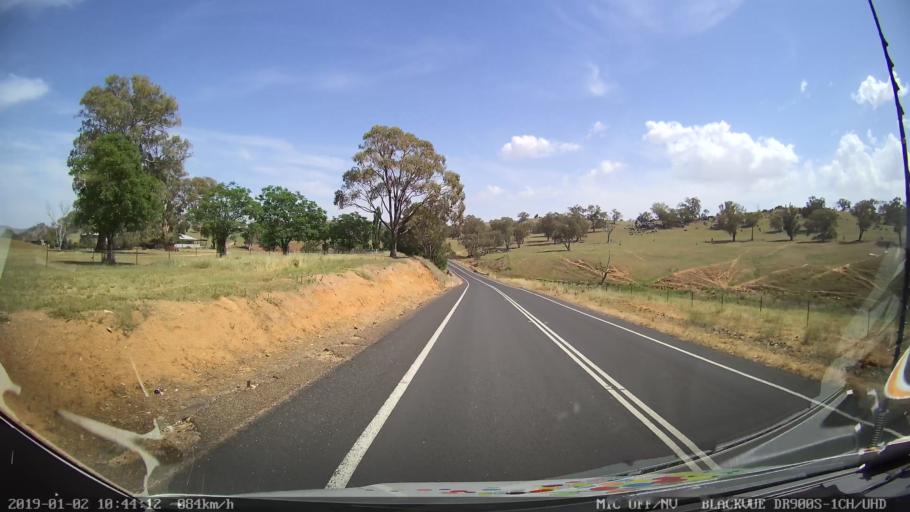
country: AU
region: New South Wales
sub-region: Cootamundra
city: Cootamundra
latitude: -34.7633
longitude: 148.2980
